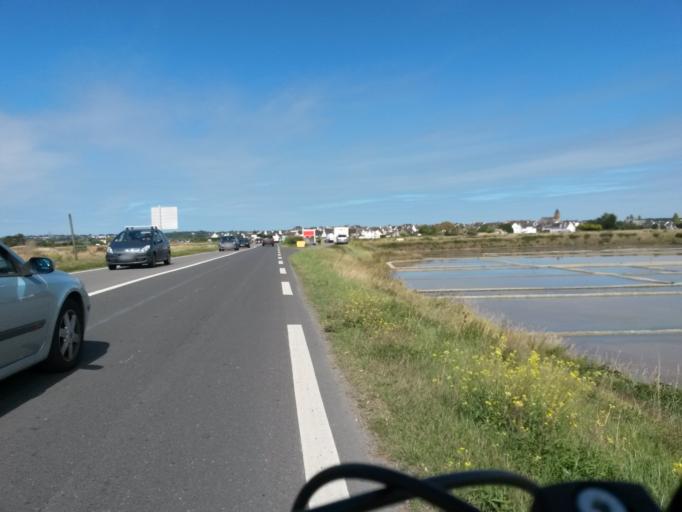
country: FR
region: Pays de la Loire
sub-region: Departement de la Loire-Atlantique
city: Le Pouliguen
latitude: 47.2916
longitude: -2.4381
